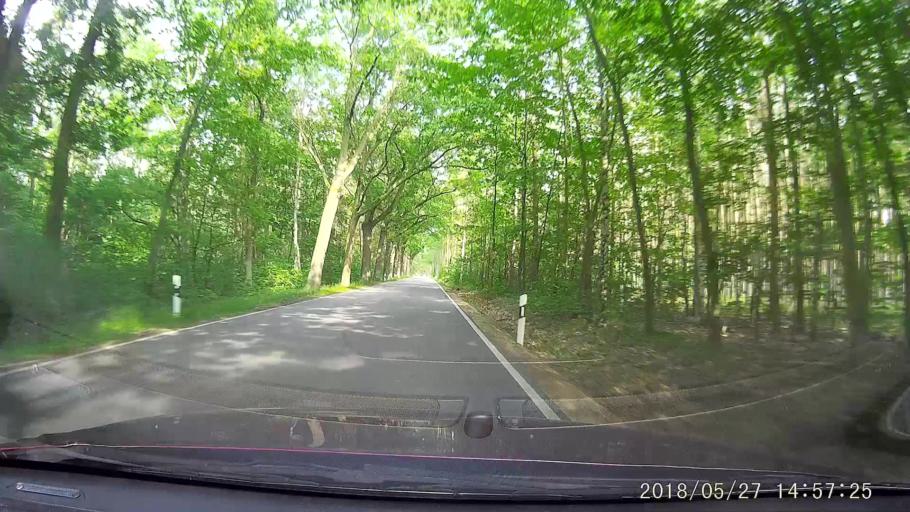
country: DE
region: Saxony
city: Klitten
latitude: 51.3454
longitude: 14.6527
